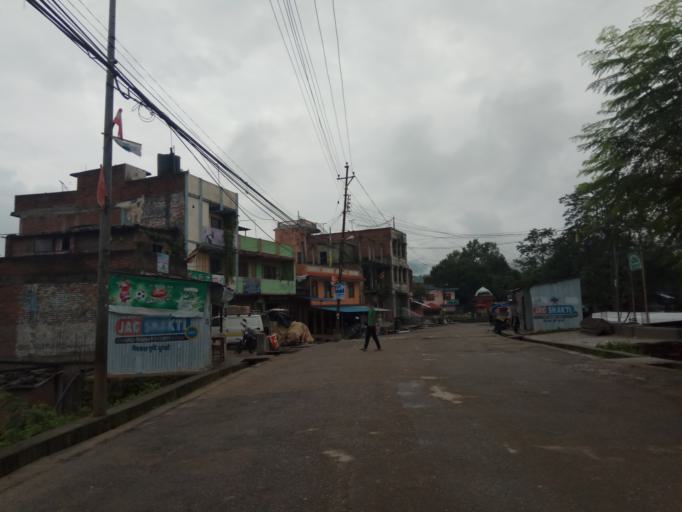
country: NP
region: Central Region
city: Kirtipur
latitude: 27.9091
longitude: 84.9000
